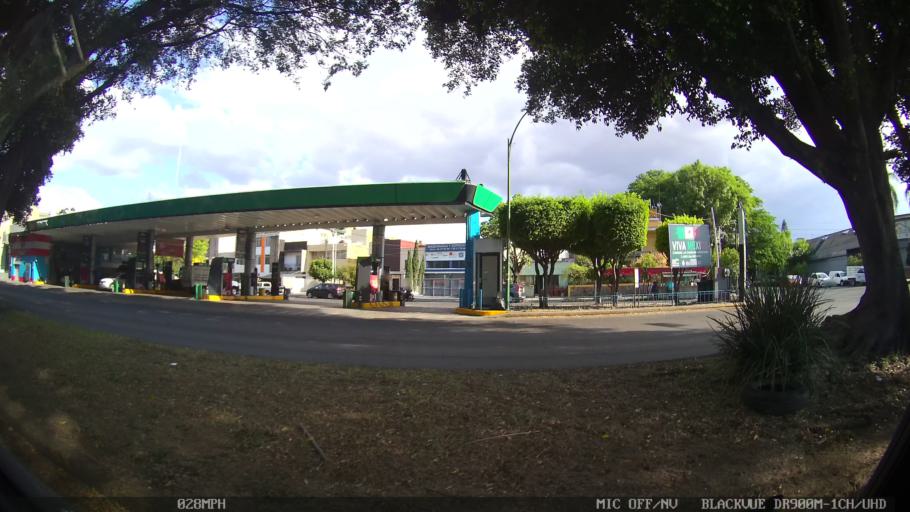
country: MX
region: Jalisco
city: Guadalajara
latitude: 20.6666
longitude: -103.3616
